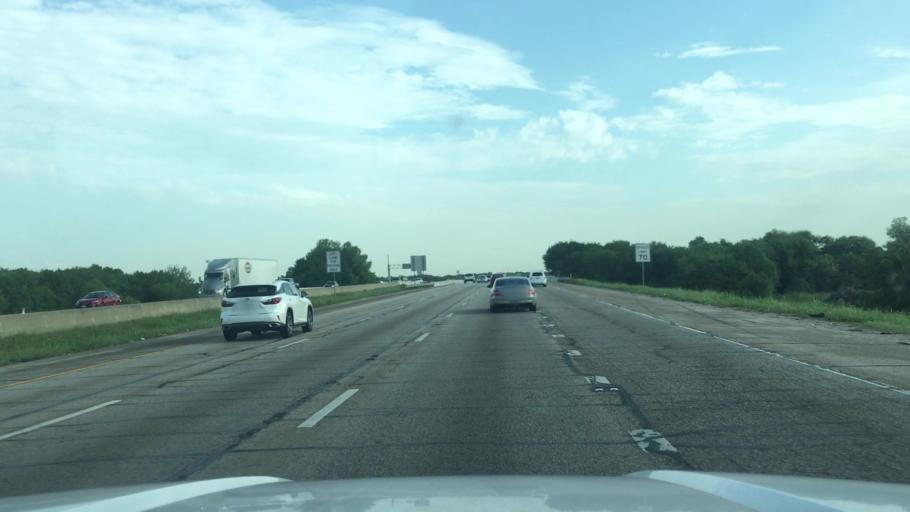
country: US
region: Texas
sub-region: Dallas County
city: Irving
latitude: 32.7915
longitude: -96.9198
